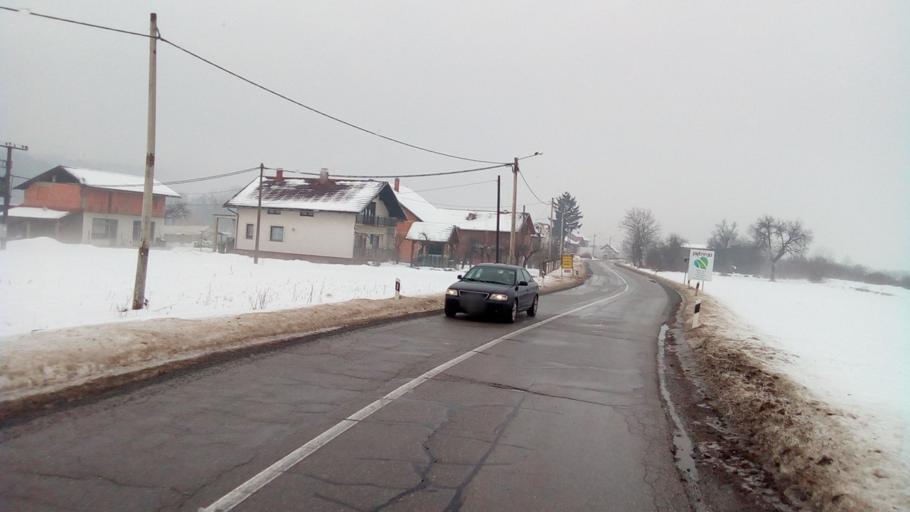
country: HR
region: Sisacko-Moslavacka
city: Petrinja
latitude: 45.4131
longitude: 16.2957
